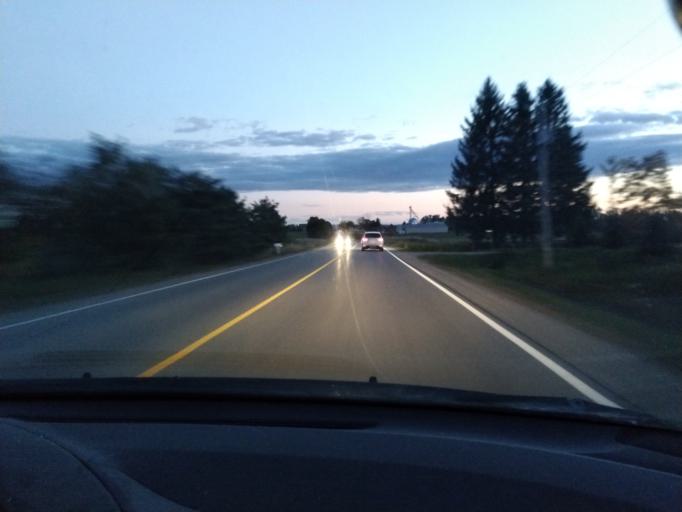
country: CA
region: Ontario
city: Bradford West Gwillimbury
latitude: 44.1286
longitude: -79.6466
